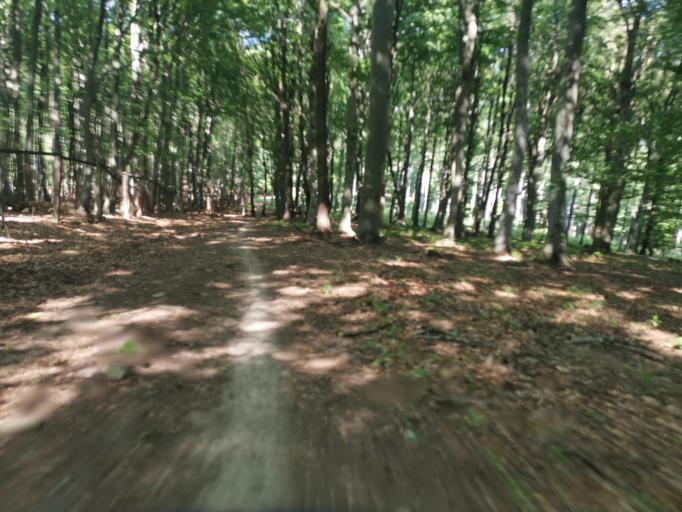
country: CZ
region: South Moravian
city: Knezdub
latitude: 48.8225
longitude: 17.4096
